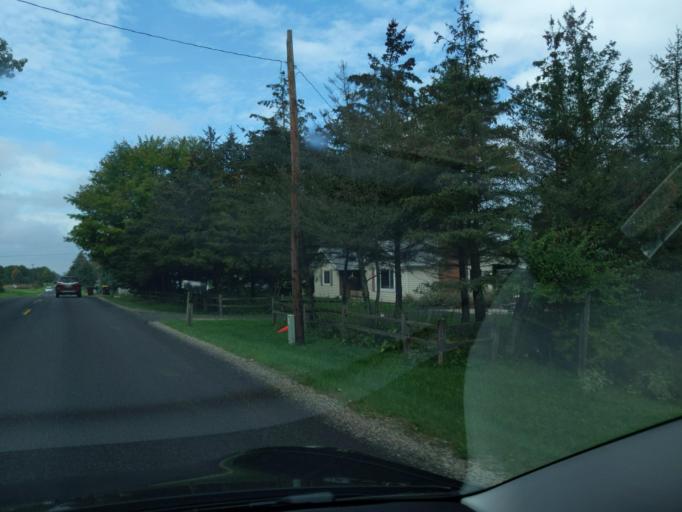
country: US
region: Michigan
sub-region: Eaton County
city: Dimondale
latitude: 42.6257
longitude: -84.6512
